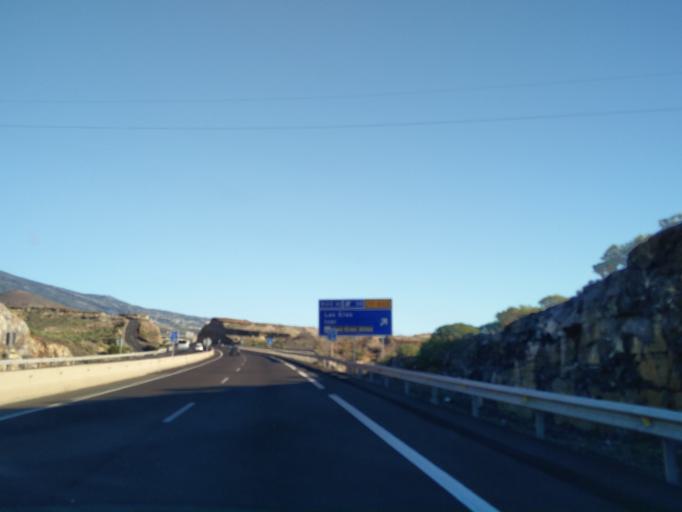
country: ES
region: Canary Islands
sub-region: Provincia de Santa Cruz de Tenerife
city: Fasnia
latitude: 28.1956
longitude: -16.4265
